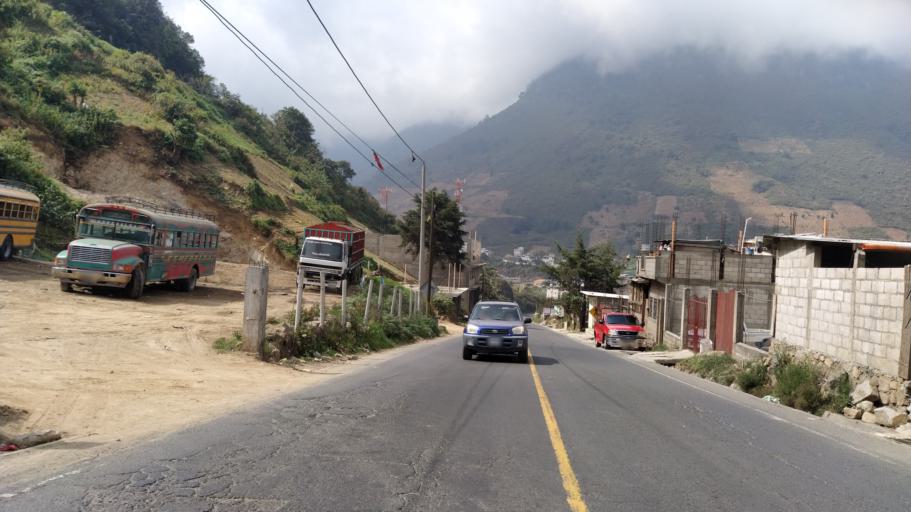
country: GT
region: Quetzaltenango
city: Zunil
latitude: 14.7821
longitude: -91.4865
